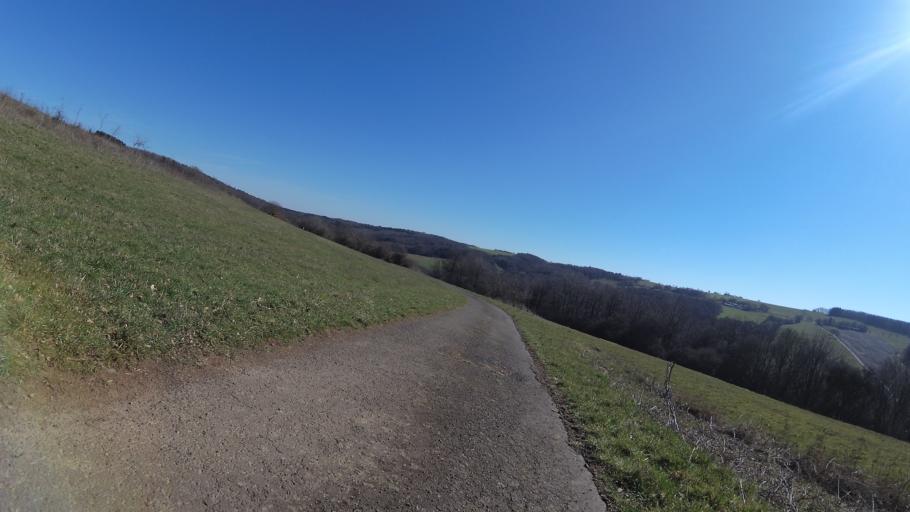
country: DE
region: Rheinland-Pfalz
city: Breitenbach
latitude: 49.4520
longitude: 7.2509
